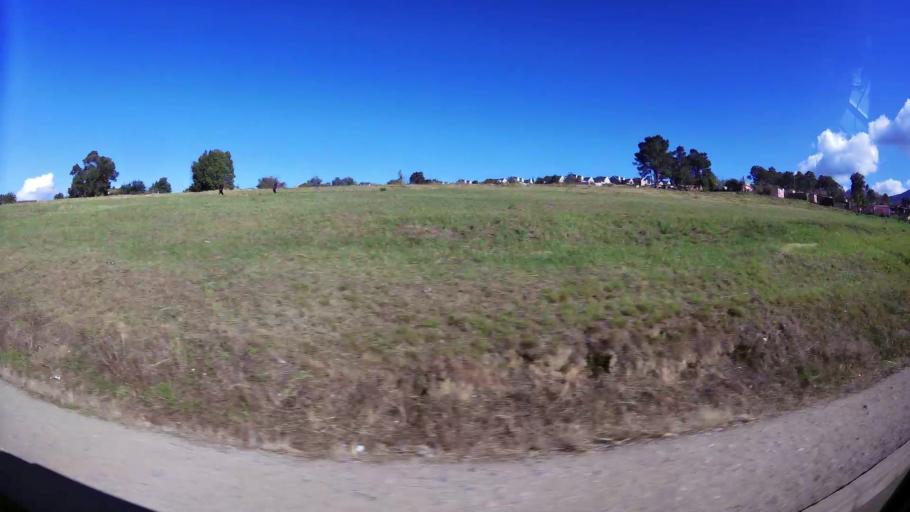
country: ZA
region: Western Cape
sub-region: Eden District Municipality
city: George
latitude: -33.9419
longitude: 22.4111
